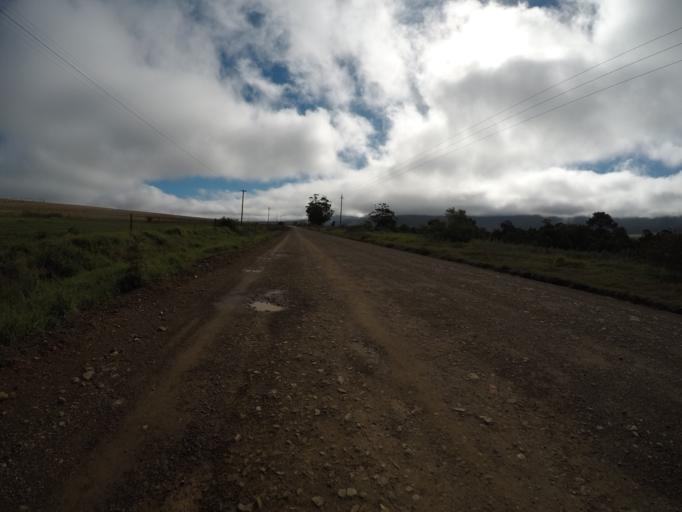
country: ZA
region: Western Cape
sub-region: Cape Winelands District Municipality
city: Ashton
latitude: -34.1361
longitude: 19.8586
